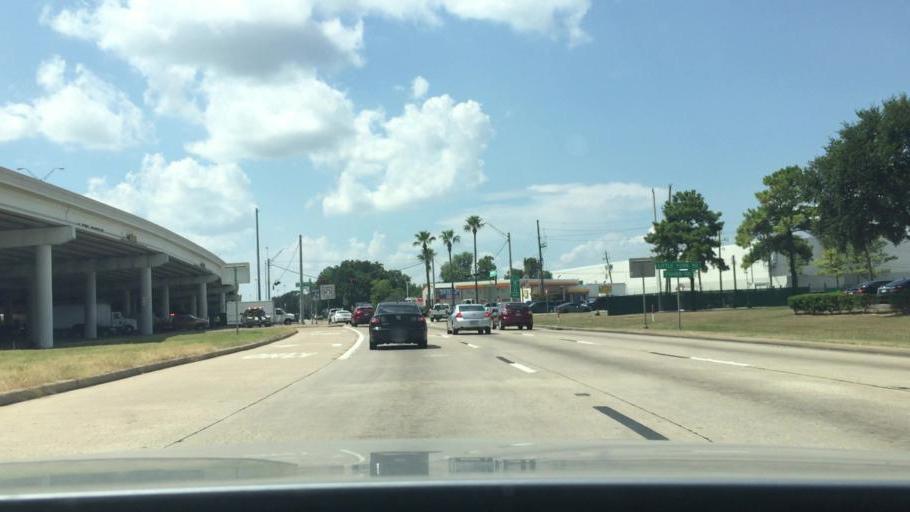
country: US
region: Texas
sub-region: Harris County
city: Jersey Village
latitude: 29.8683
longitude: -95.5643
